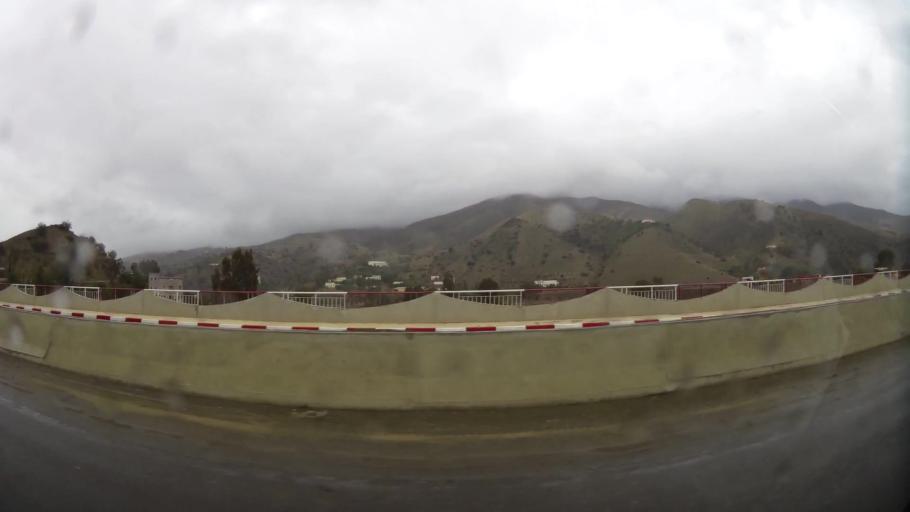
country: MA
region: Taza-Al Hoceima-Taounate
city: Imzourene
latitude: 35.0192
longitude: -3.8206
